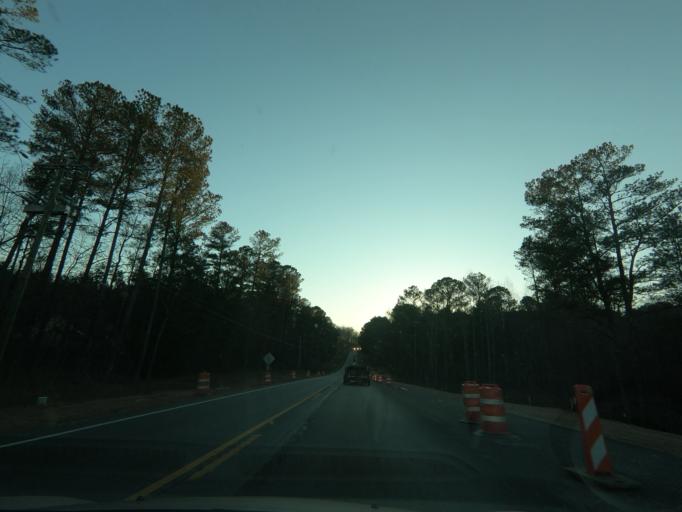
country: US
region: Georgia
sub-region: Forsyth County
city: Cumming
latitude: 34.3058
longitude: -84.2164
